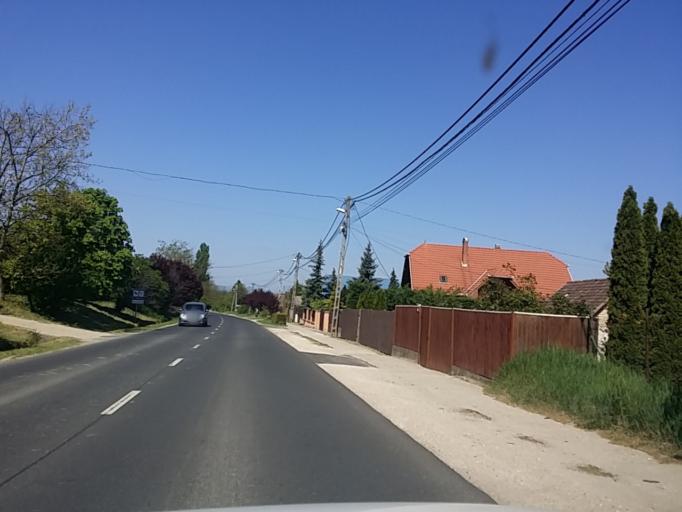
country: HU
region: Pest
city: Mogyorod
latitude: 47.5994
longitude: 19.2580
